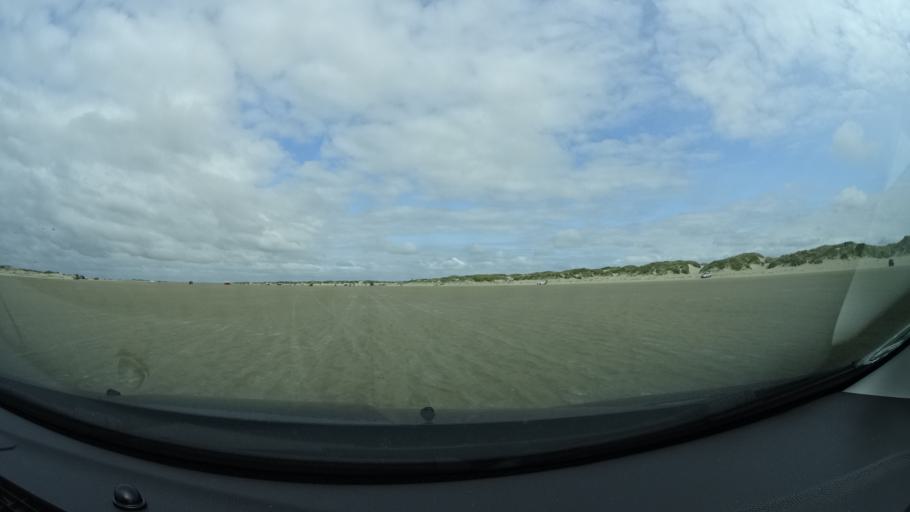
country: DE
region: Schleswig-Holstein
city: List
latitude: 55.1410
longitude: 8.4840
